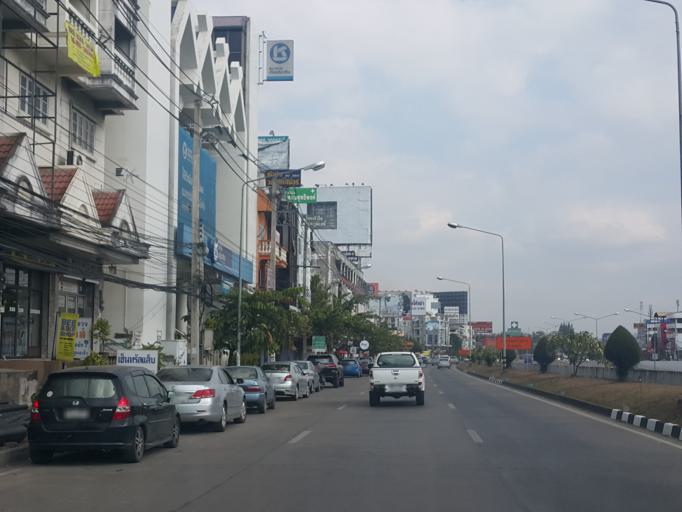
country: TH
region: Chiang Mai
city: Chiang Mai
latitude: 18.8122
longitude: 98.9845
